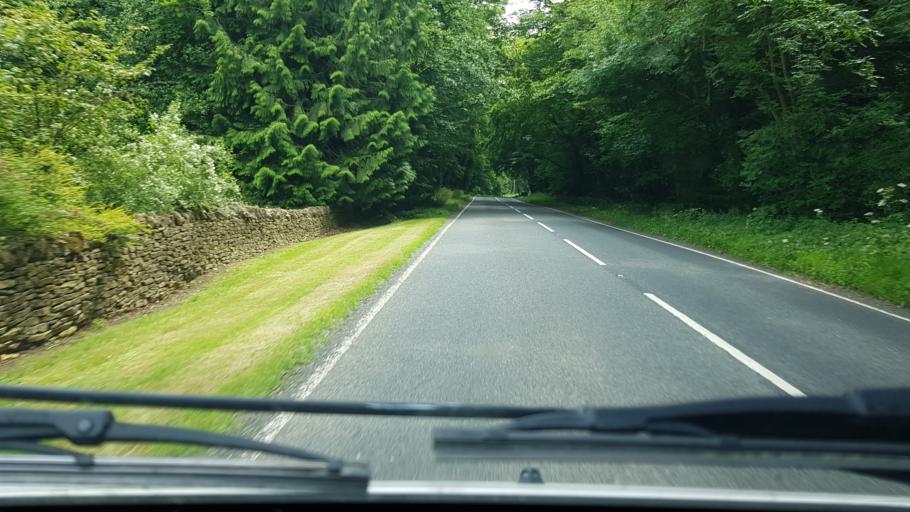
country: GB
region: England
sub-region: Gloucestershire
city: Donnington
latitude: 51.9836
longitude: -1.7681
